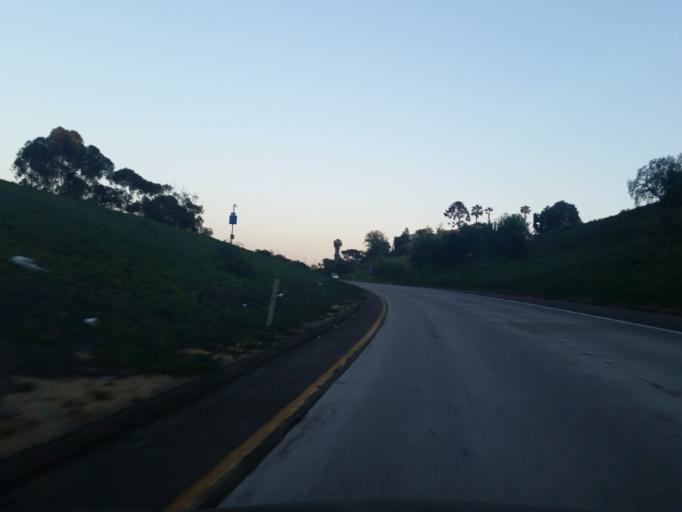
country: US
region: California
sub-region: San Diego County
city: San Diego
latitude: 32.7366
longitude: -117.1153
